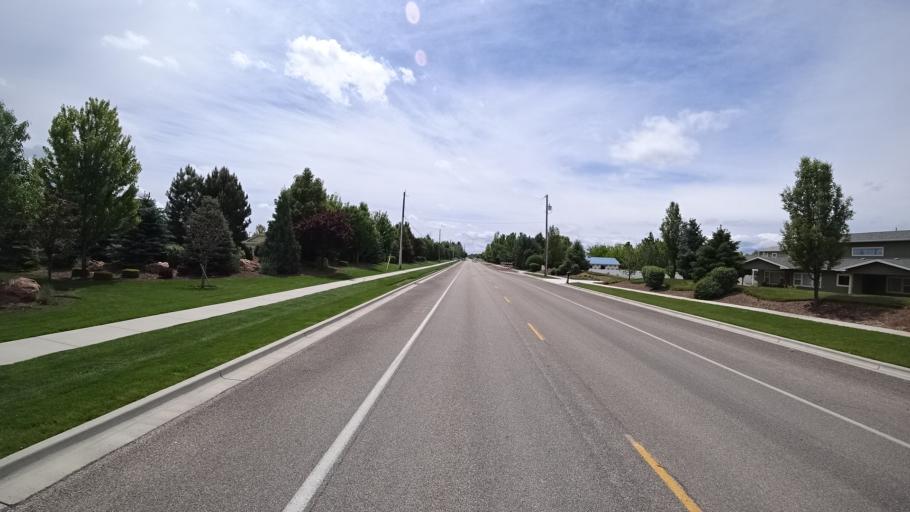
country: US
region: Idaho
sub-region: Ada County
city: Eagle
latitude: 43.7123
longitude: -116.4035
